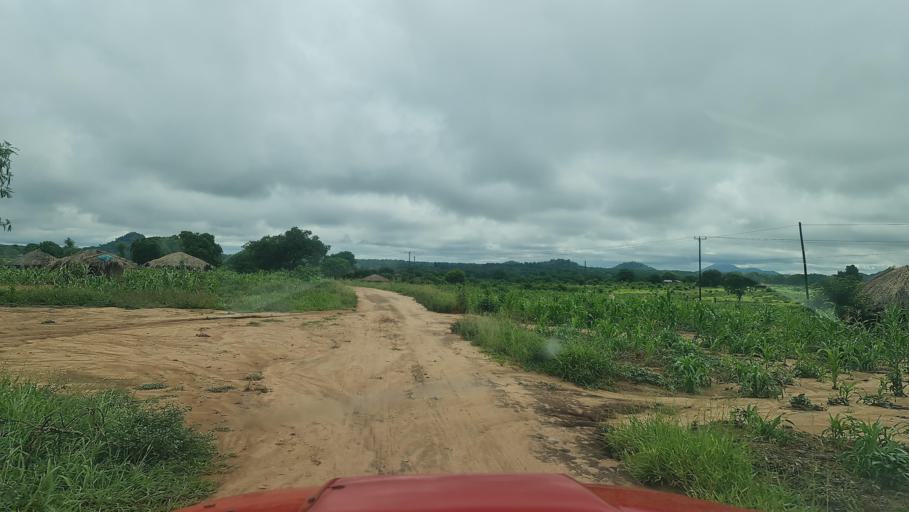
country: MW
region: Southern Region
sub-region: Nsanje District
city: Nsanje
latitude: -17.1858
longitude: 35.9235
